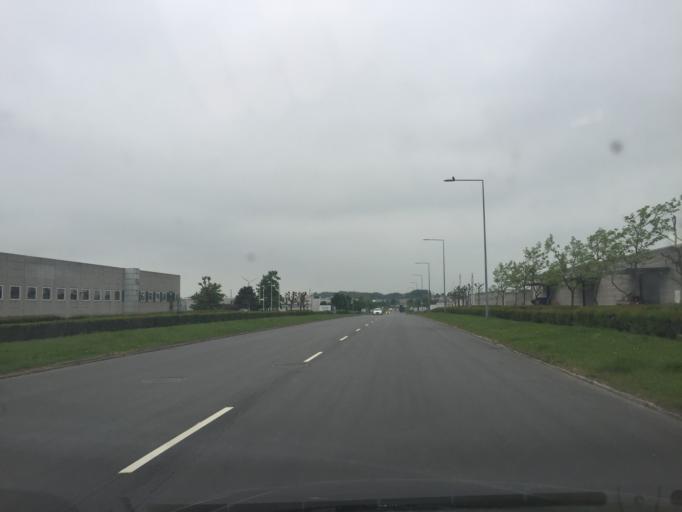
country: DK
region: Capital Region
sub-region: Hoje-Taastrup Kommune
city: Taastrup
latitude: 55.6622
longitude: 12.3049
